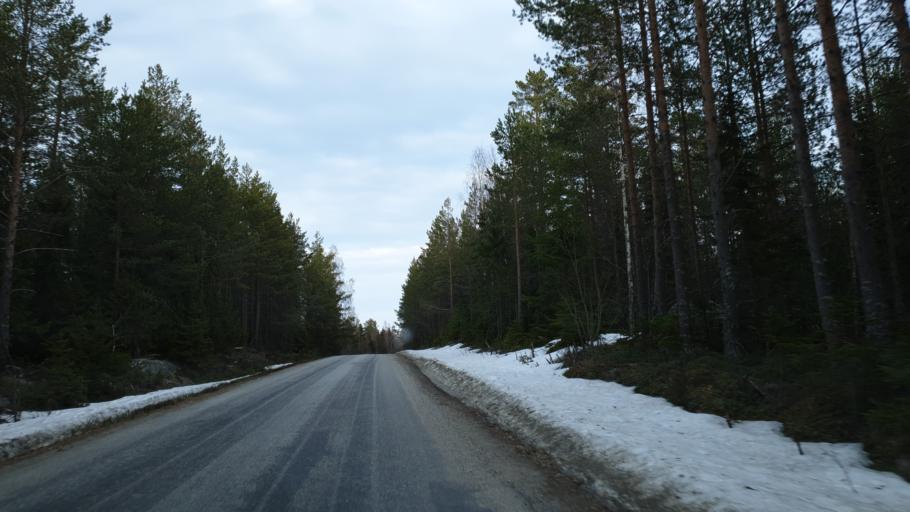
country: SE
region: Gaevleborg
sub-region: Nordanstigs Kommun
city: Bergsjoe
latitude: 61.9590
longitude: 17.3508
